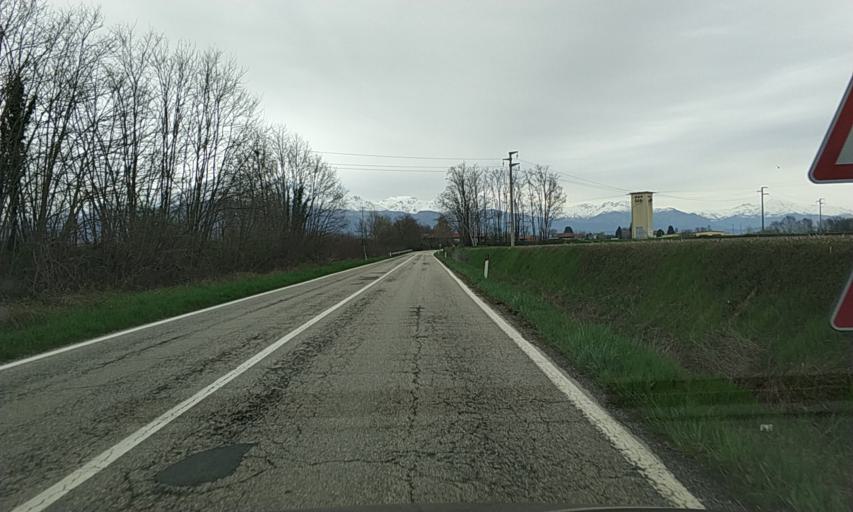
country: IT
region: Piedmont
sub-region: Provincia di Torino
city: Favria
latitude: 45.3114
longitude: 7.6782
